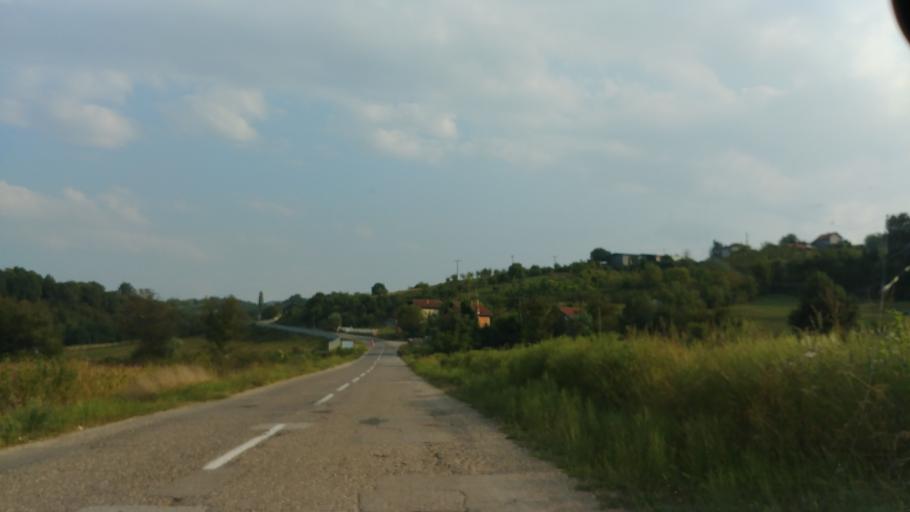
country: BA
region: Republika Srpska
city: Lopare
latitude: 44.7159
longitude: 18.8842
